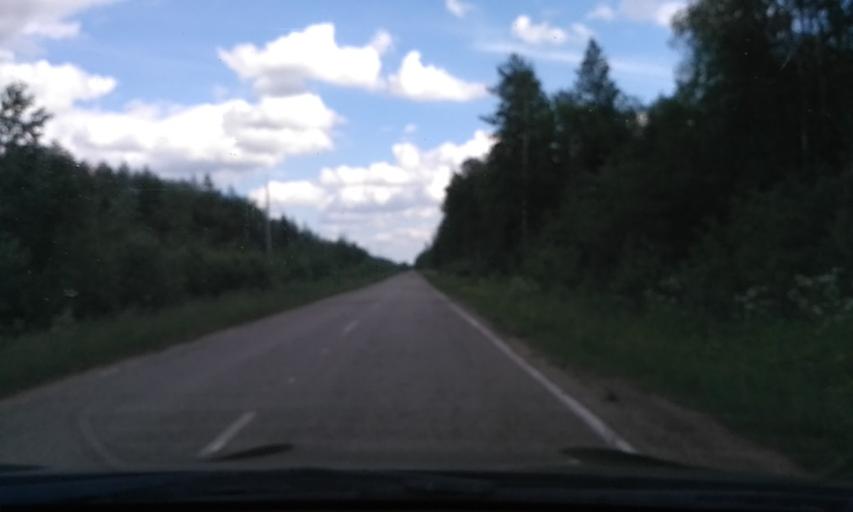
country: RU
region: Leningrad
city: Otradnoye
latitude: 59.8209
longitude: 30.7878
